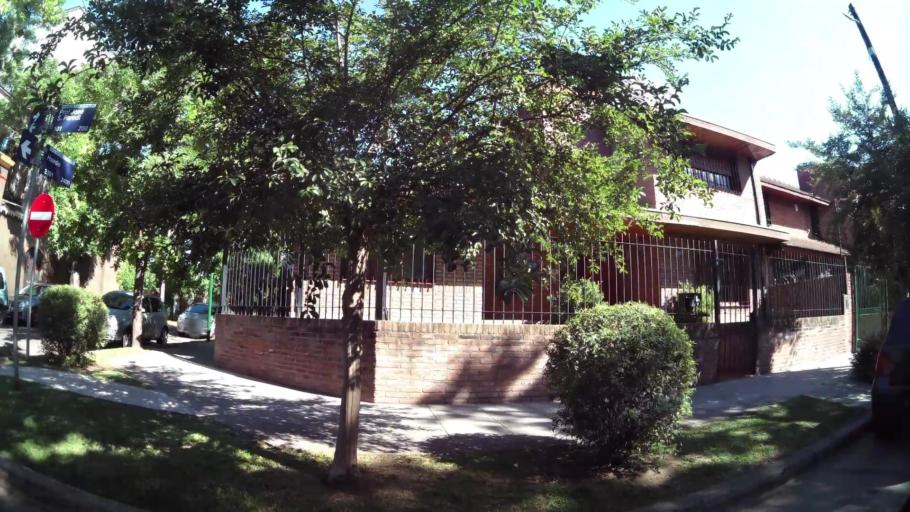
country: AR
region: Buenos Aires
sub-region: Partido de San Isidro
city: San Isidro
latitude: -34.4581
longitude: -58.5330
